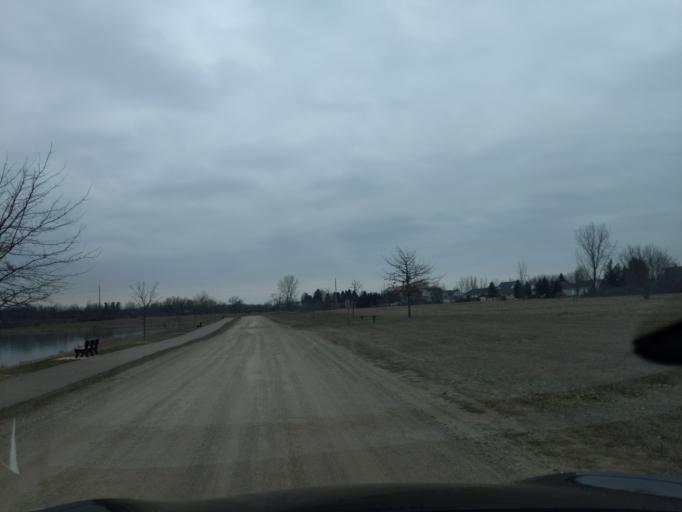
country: US
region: Michigan
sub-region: Eaton County
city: Potterville
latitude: 42.6201
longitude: -84.7525
